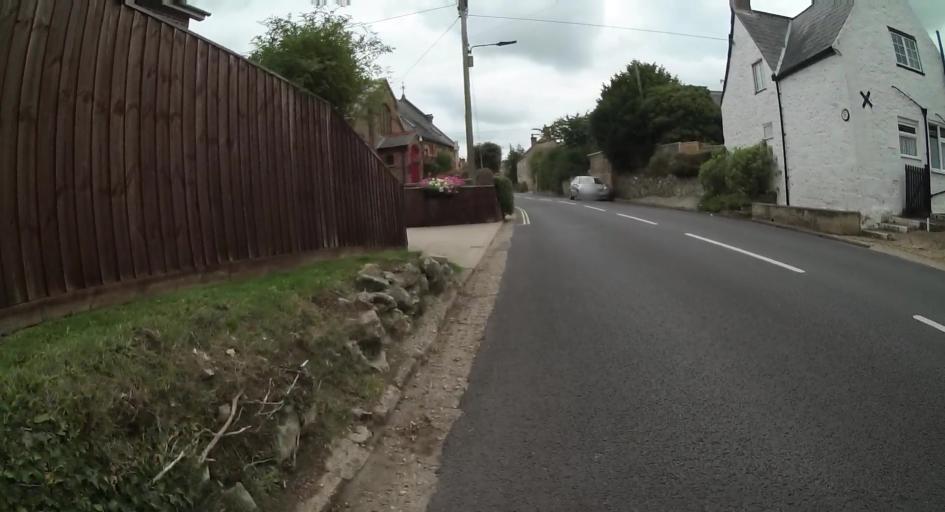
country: GB
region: England
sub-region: Isle of Wight
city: Niton
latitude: 50.6004
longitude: -1.2657
